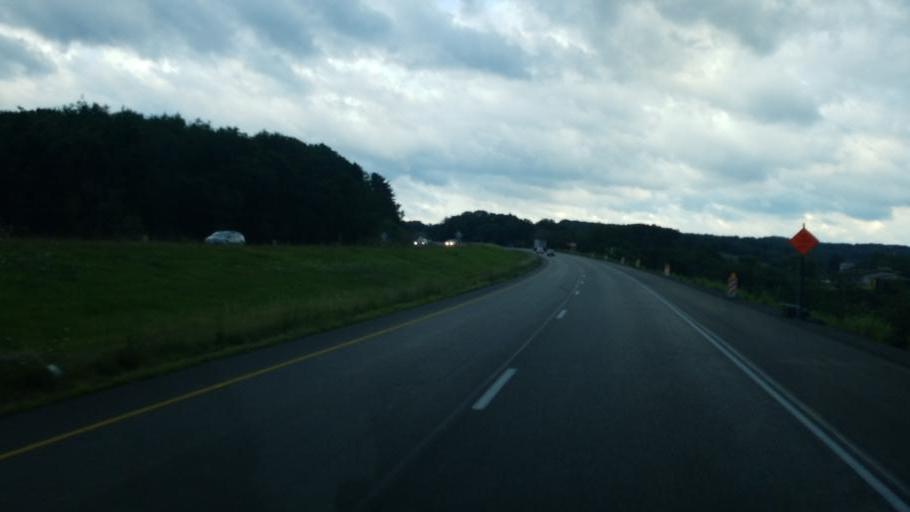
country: US
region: Pennsylvania
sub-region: Butler County
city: Zelienople
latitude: 40.7708
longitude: -80.1295
